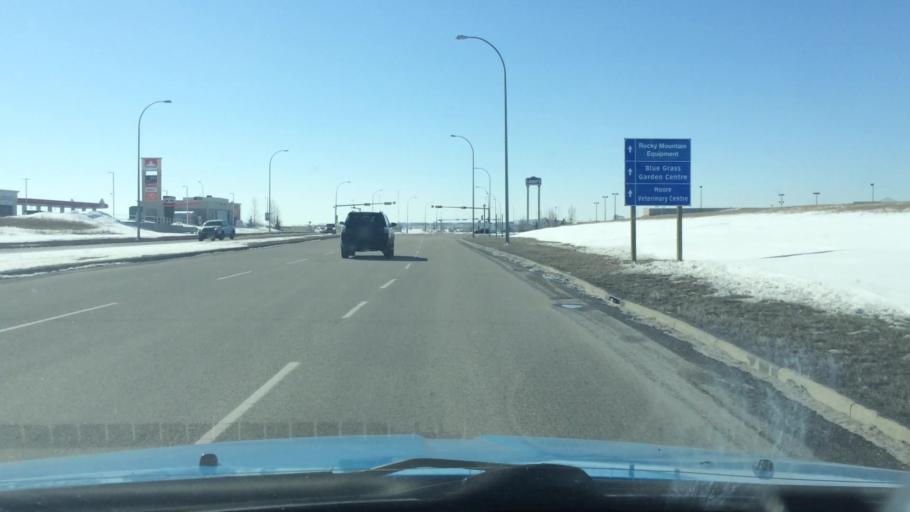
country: CA
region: Alberta
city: Airdrie
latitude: 51.2116
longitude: -113.9908
